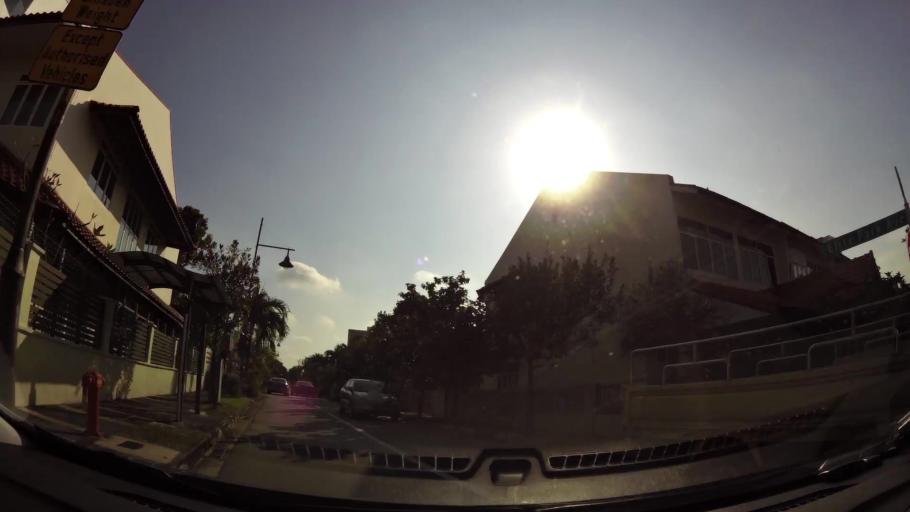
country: SG
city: Singapore
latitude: 1.3147
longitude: 103.9229
